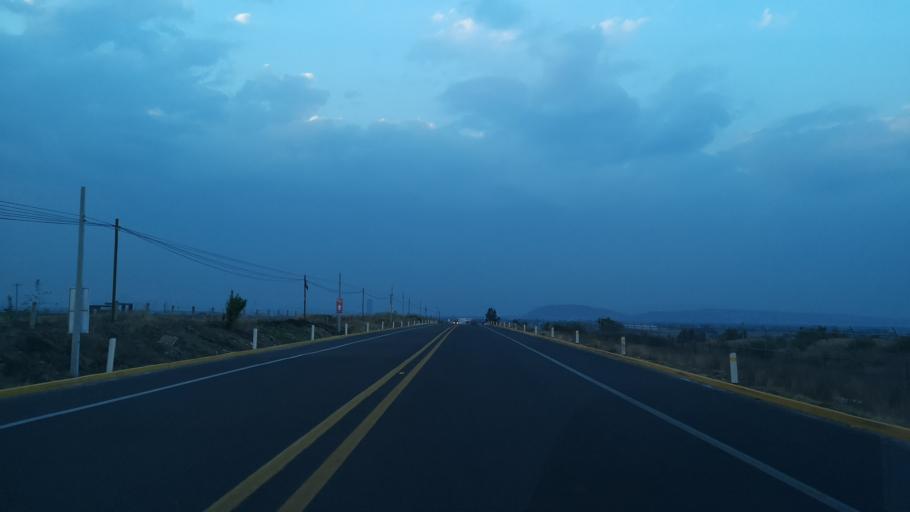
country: MX
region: Puebla
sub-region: Huejotzingo
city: Los Encinos
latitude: 19.1748
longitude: -98.3742
